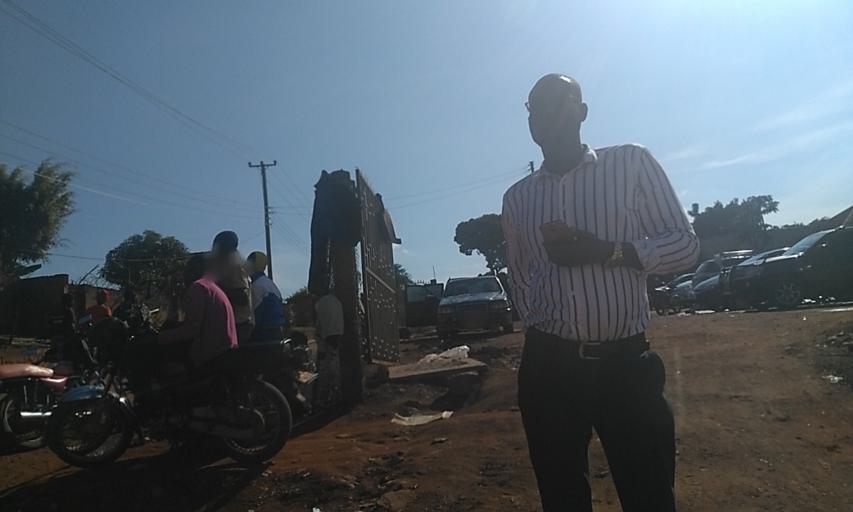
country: UG
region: Central Region
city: Kampala Central Division
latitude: 0.3219
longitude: 32.5440
